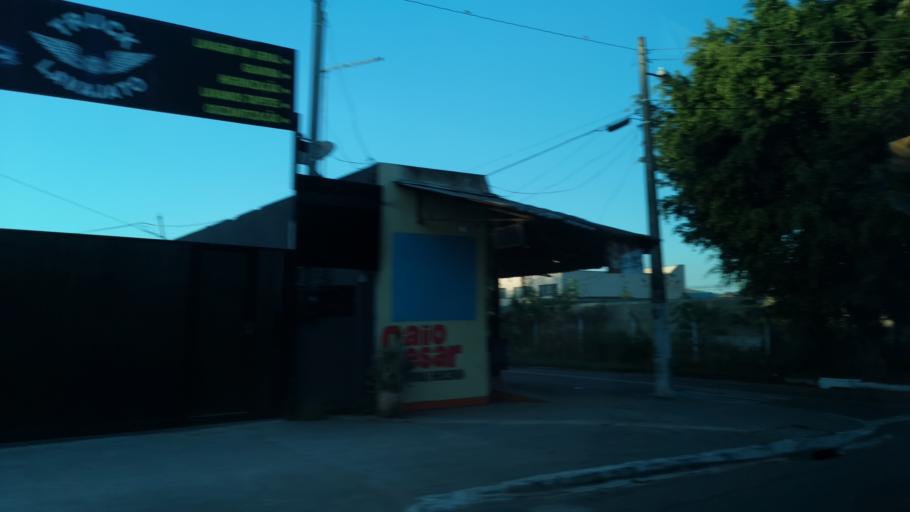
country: BR
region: Goias
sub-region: Goiania
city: Goiania
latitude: -16.6941
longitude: -49.1894
